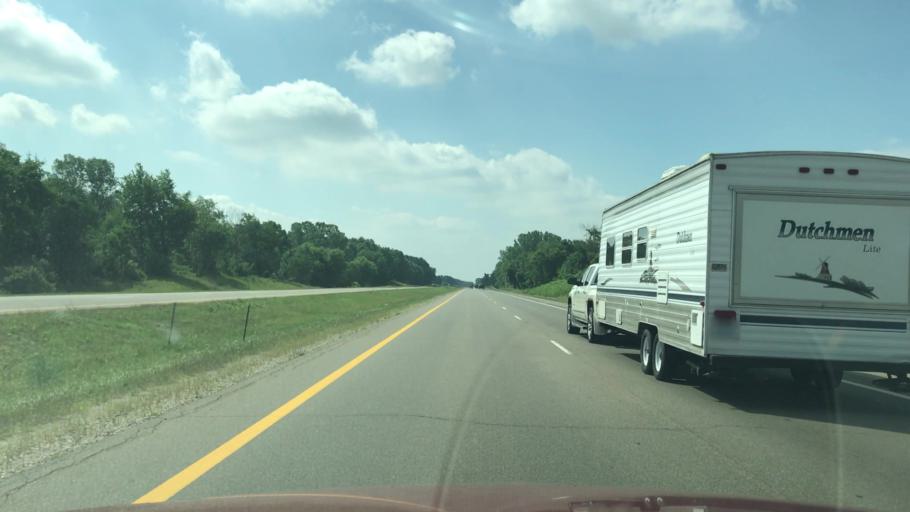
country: US
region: Michigan
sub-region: Kent County
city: Sparta
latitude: 43.1145
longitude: -85.7043
